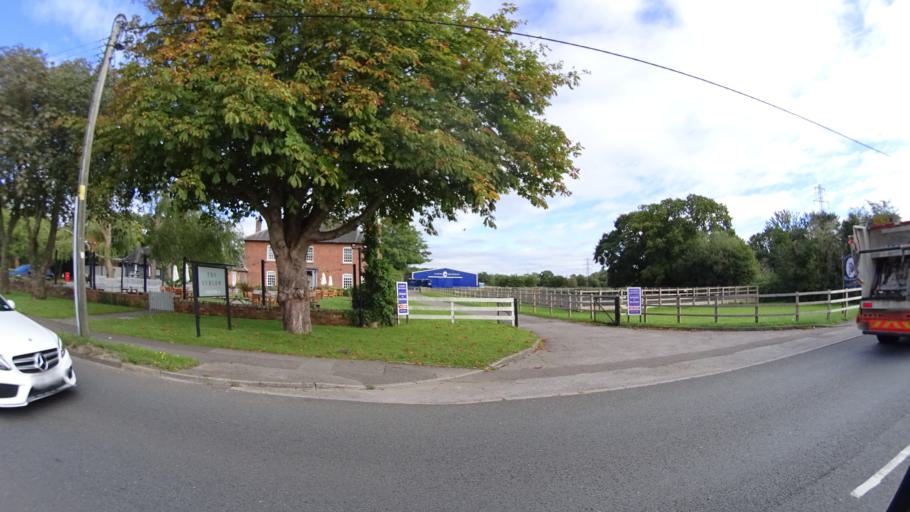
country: GB
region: England
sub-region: Dorset
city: Ferndown
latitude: 50.7815
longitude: -1.8757
